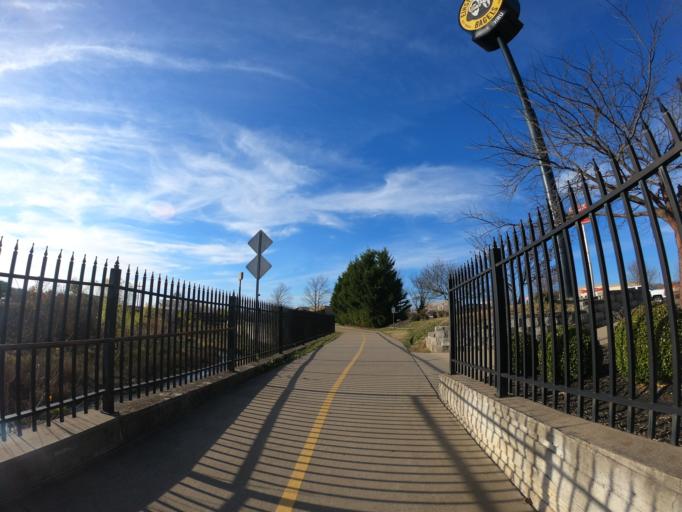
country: US
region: Arkansas
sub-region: Benton County
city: Bentonville
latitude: 36.3150
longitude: -94.1823
